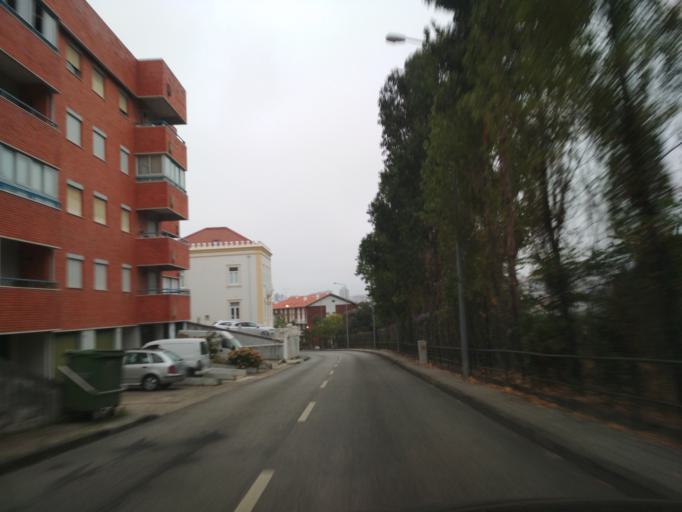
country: PT
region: Coimbra
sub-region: Coimbra
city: Coimbra
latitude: 40.1980
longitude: -8.4359
